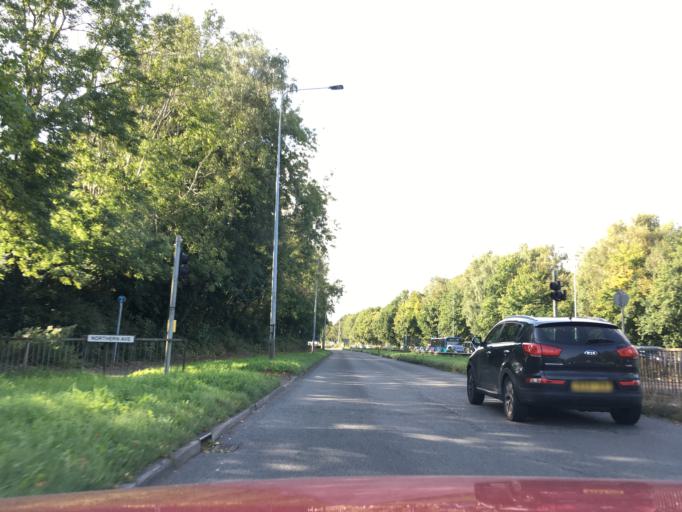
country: GB
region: Wales
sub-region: Cardiff
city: Radyr
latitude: 51.5241
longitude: -3.2303
